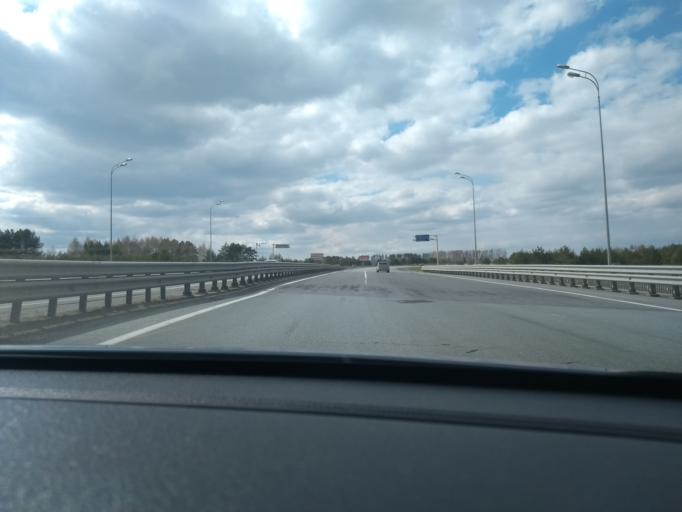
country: RU
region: Tatarstan
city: Yelabuga
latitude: 55.7820
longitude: 52.1776
